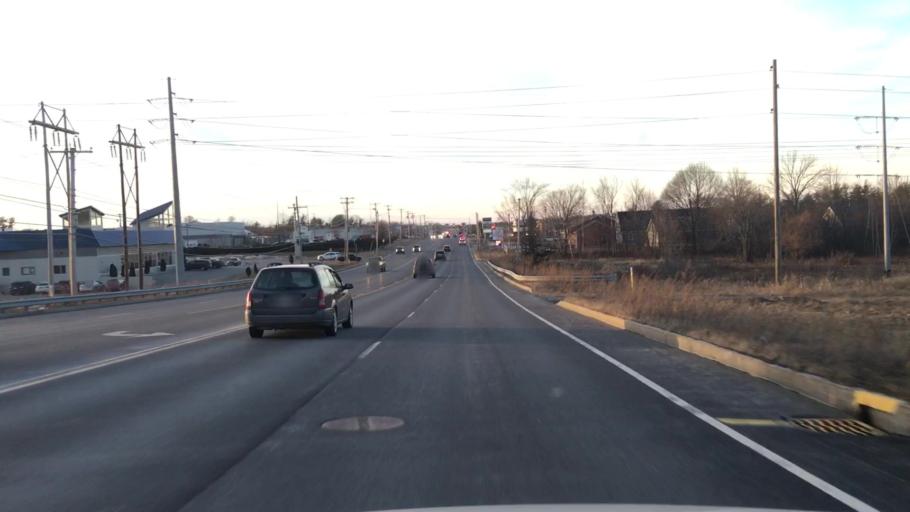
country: US
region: Maine
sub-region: Penobscot County
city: Brewer
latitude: 44.7743
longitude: -68.7284
